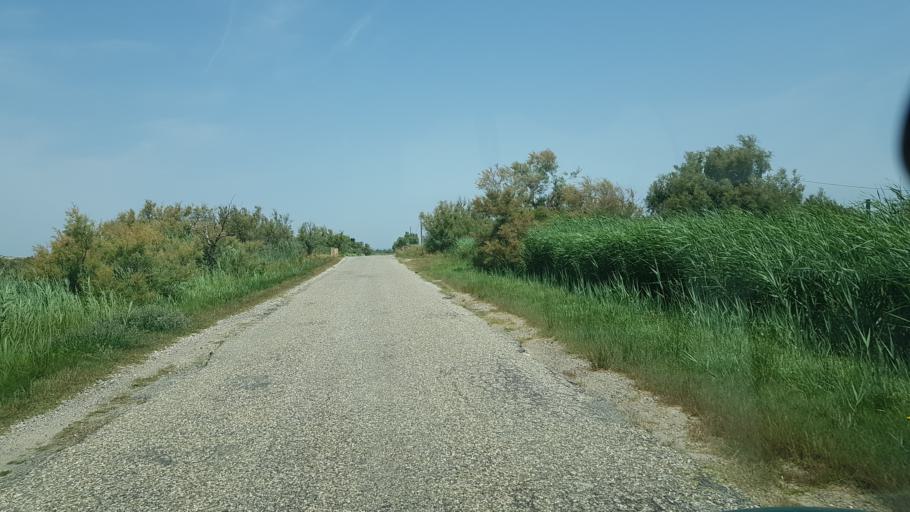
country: FR
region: Provence-Alpes-Cote d'Azur
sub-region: Departement des Bouches-du-Rhone
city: Arles
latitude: 43.5226
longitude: 4.6362
